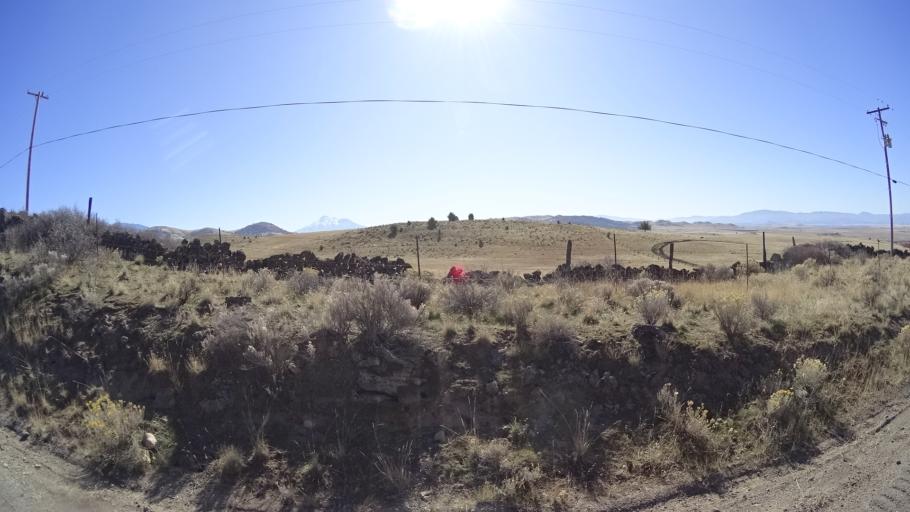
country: US
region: California
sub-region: Siskiyou County
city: Montague
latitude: 41.8326
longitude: -122.3811
